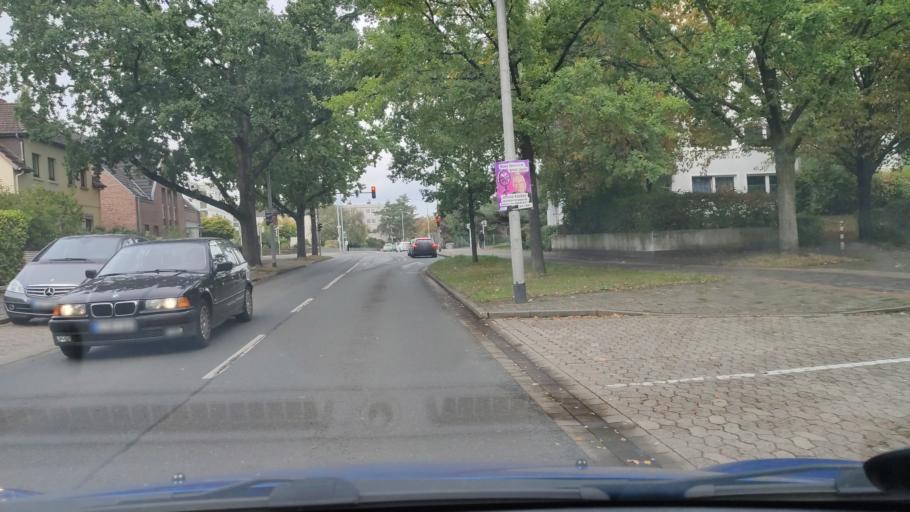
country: DE
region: Lower Saxony
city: Ronnenberg
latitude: 52.3642
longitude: 9.6698
